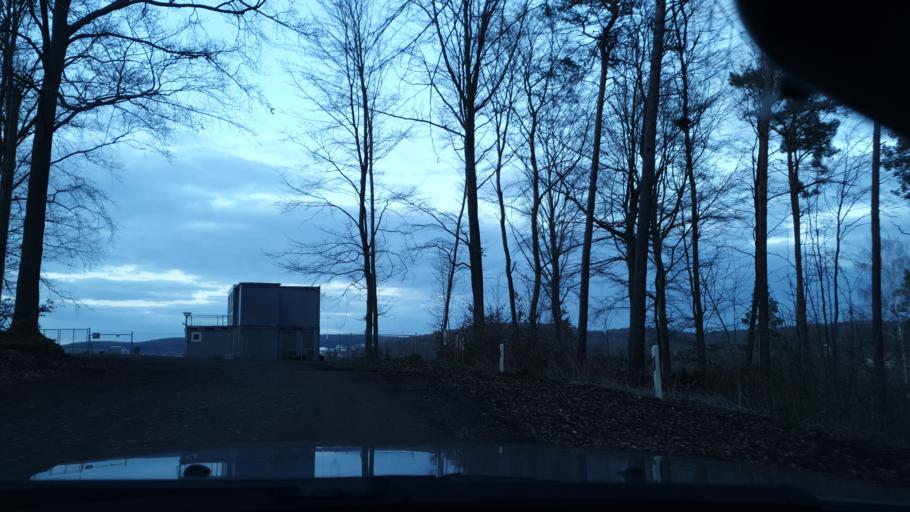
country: DE
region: Rheinland-Pfalz
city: Kaiserslautern
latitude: 49.4377
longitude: 7.7925
